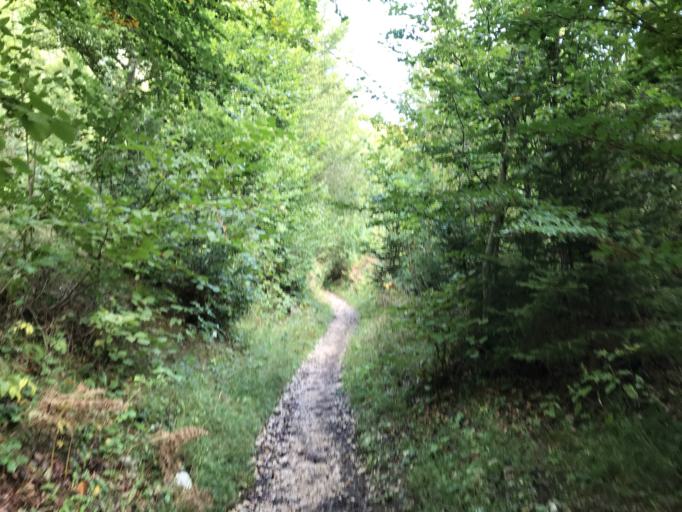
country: AT
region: Carinthia
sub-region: Villach Stadt
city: Villach
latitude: 46.5838
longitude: 13.8156
